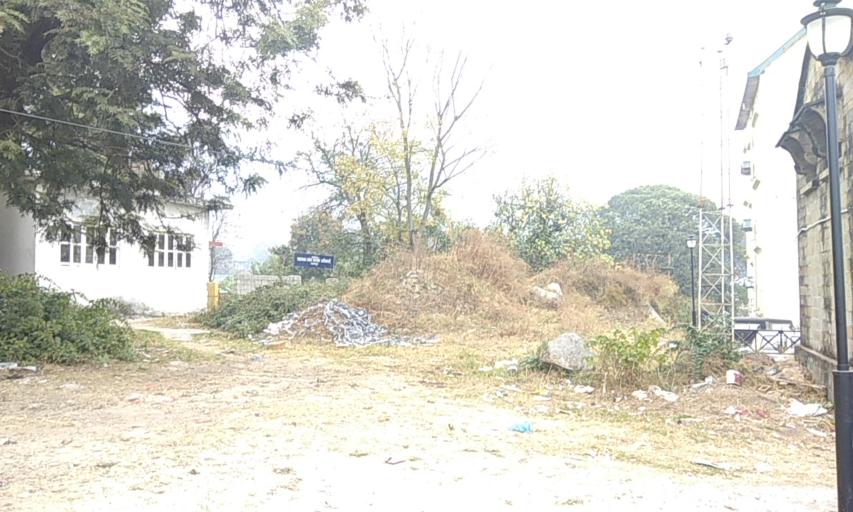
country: IN
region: Himachal Pradesh
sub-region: Kangra
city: Palampur
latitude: 32.1100
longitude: 76.5368
